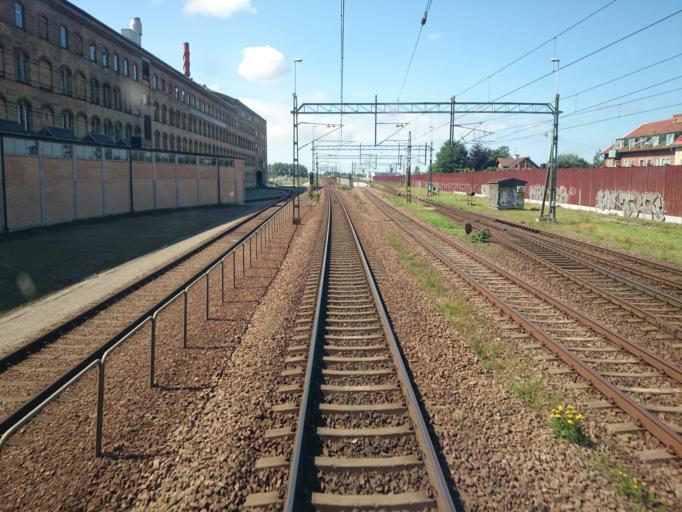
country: SE
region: Skane
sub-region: Burlovs Kommun
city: Arloev
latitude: 55.6333
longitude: 13.0676
